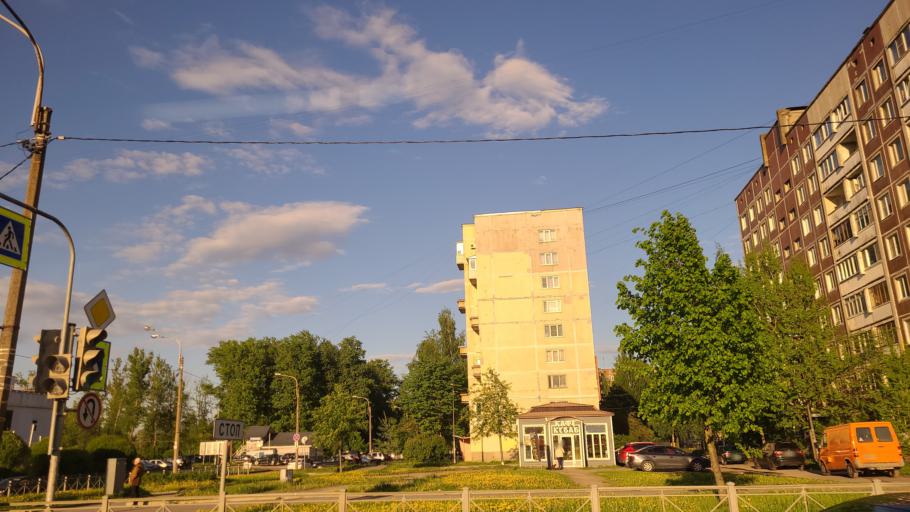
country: RU
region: St.-Petersburg
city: Kolpino
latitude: 59.7379
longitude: 30.5800
